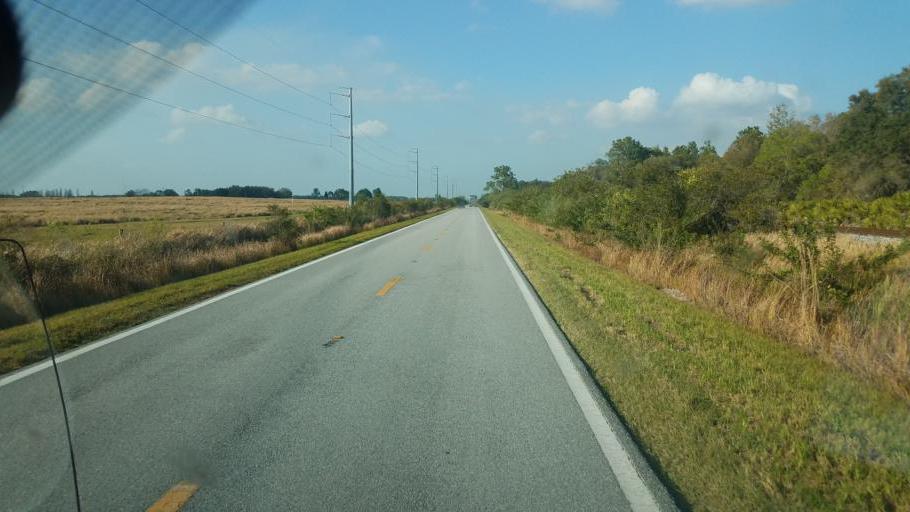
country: US
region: Florida
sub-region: Hardee County
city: Bowling Green
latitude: 27.6546
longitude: -81.9502
